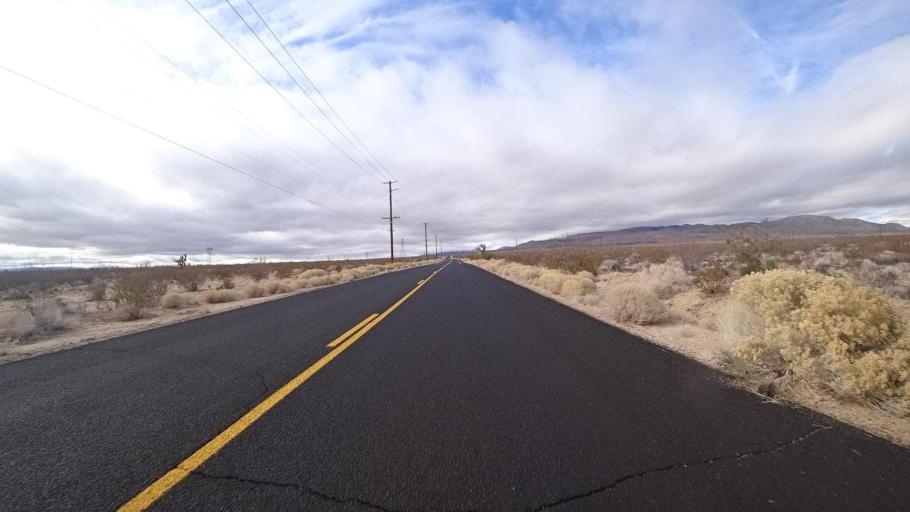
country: US
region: California
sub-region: Kern County
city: Mojave
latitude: 34.9509
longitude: -118.3061
